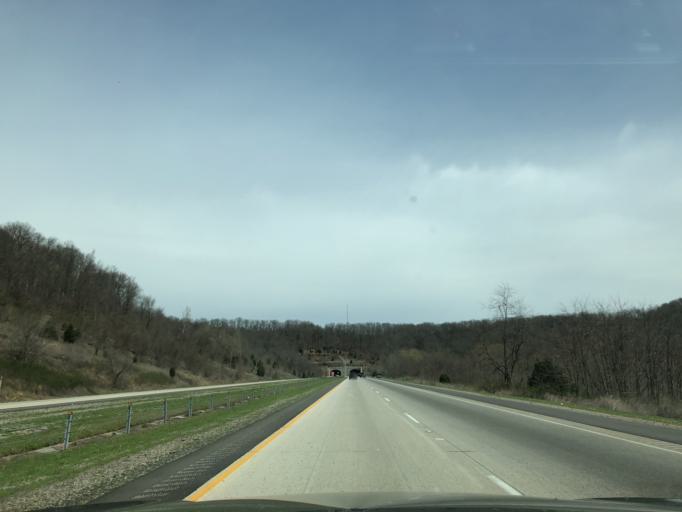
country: US
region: Arkansas
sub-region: Washington County
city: West Fork
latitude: 35.7601
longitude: -94.1942
